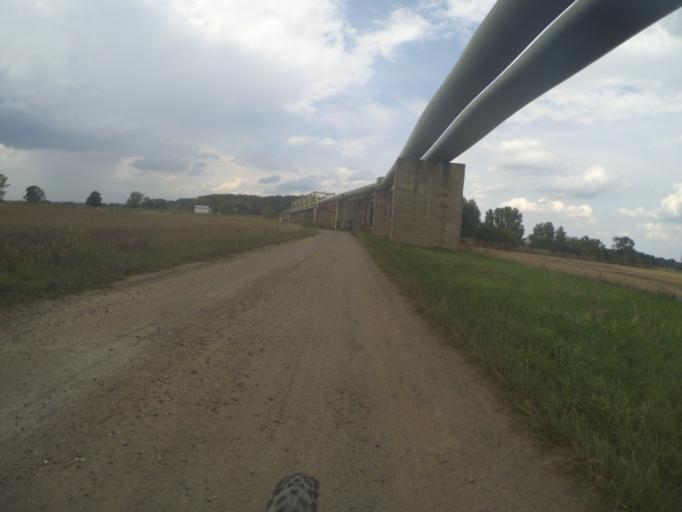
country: CZ
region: Central Bohemia
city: Luzec nad Vltavou
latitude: 50.3169
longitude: 14.4418
